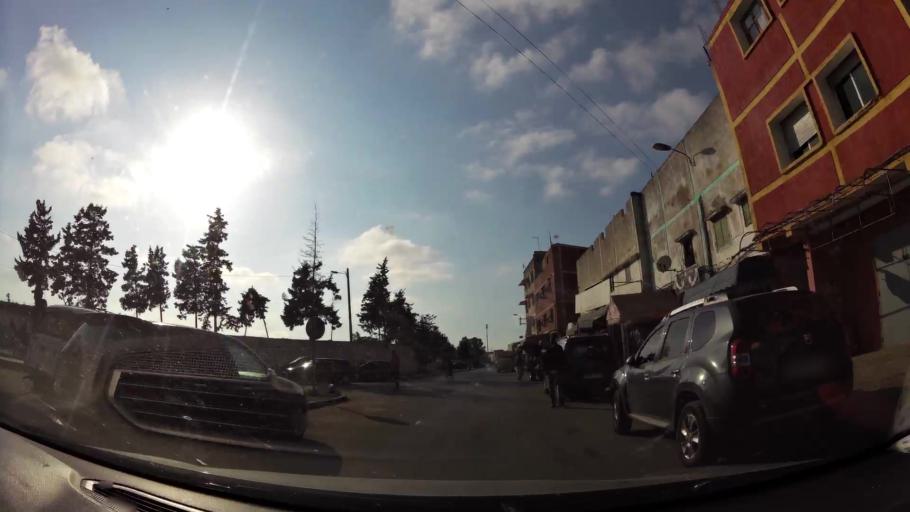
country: MA
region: Rabat-Sale-Zemmour-Zaer
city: Sale
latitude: 34.0487
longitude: -6.7840
